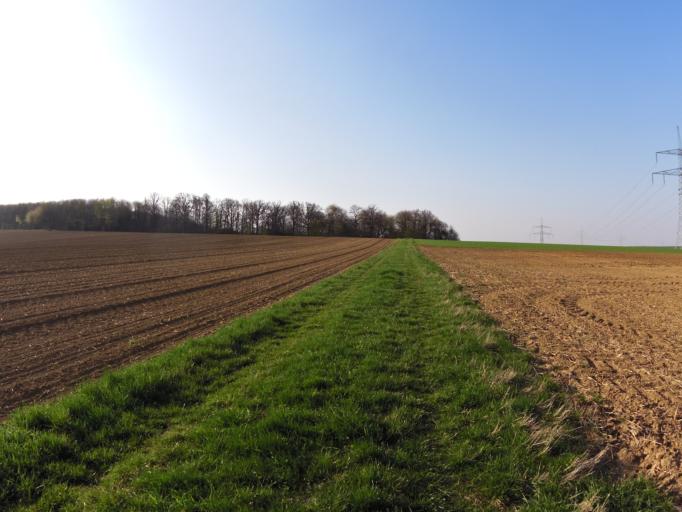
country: DE
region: Bavaria
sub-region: Regierungsbezirk Unterfranken
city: Theilheim
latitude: 49.7731
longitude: 10.0488
